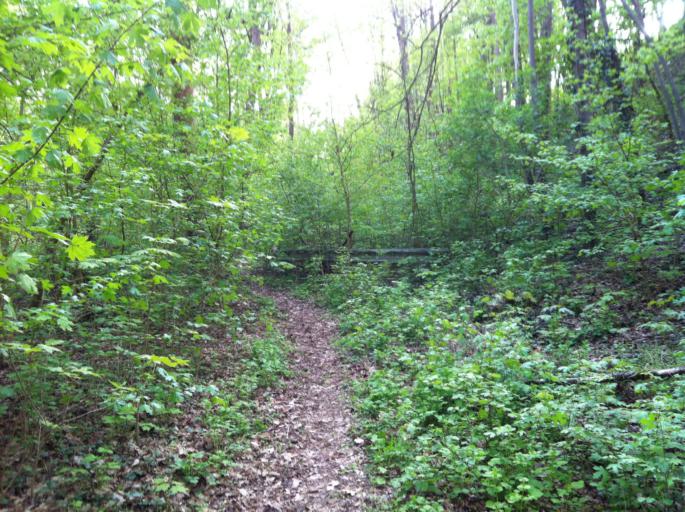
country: DE
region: Rheinland-Pfalz
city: Budenheim
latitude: 50.0033
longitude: 8.1877
